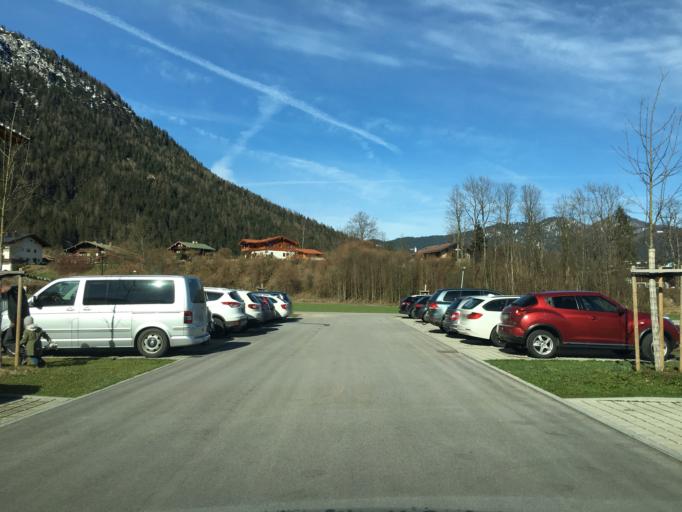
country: DE
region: Bavaria
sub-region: Upper Bavaria
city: Schoenau am Koenigssee
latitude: 47.5985
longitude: 12.9849
